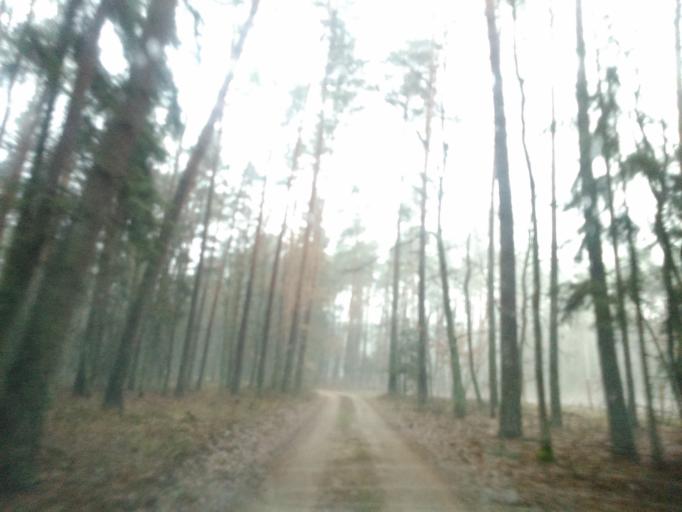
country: PL
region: Kujawsko-Pomorskie
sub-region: Powiat golubsko-dobrzynski
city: Radomin
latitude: 53.1408
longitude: 19.1318
